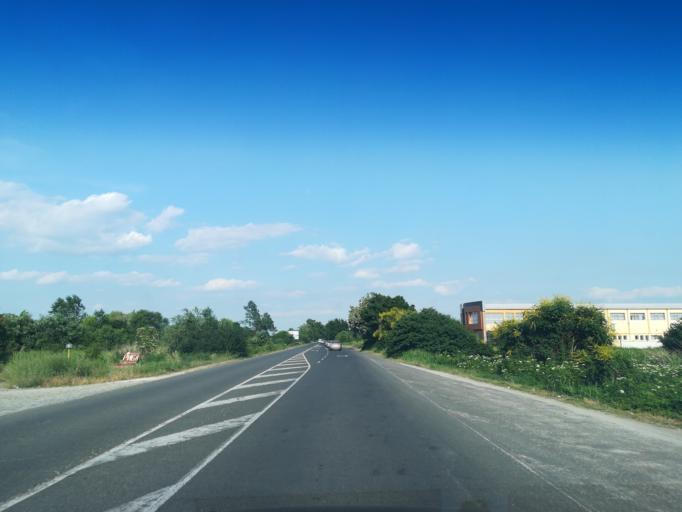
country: BG
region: Plovdiv
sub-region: Obshtina Plovdiv
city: Plovdiv
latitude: 42.1487
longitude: 24.8290
